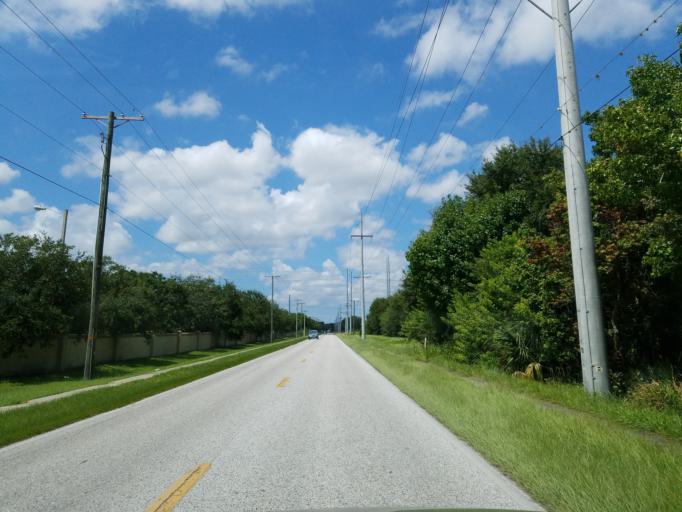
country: US
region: Florida
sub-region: Hillsborough County
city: Palm River-Clair Mel
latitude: 27.9411
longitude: -82.3404
